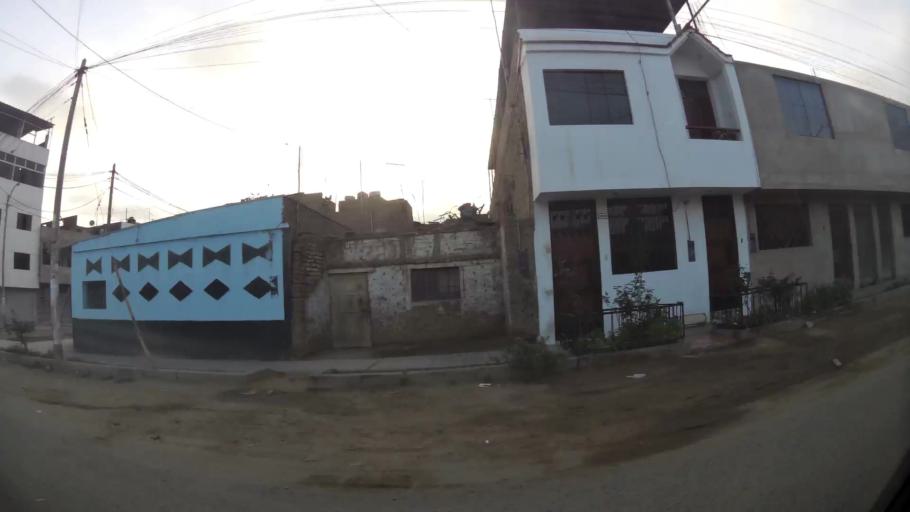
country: PE
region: La Libertad
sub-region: Provincia de Trujillo
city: El Porvenir
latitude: -8.0749
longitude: -78.9974
